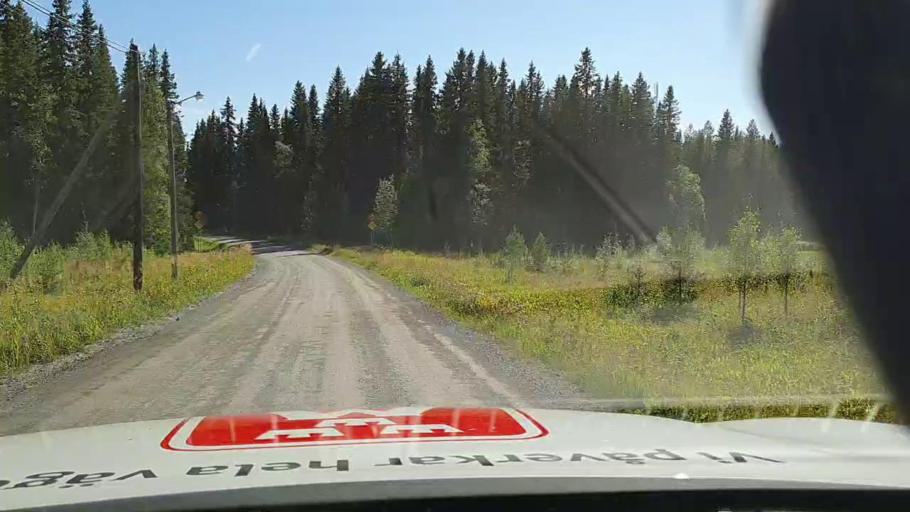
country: SE
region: Jaemtland
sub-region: Krokoms Kommun
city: Krokom
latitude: 63.6832
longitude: 14.6032
